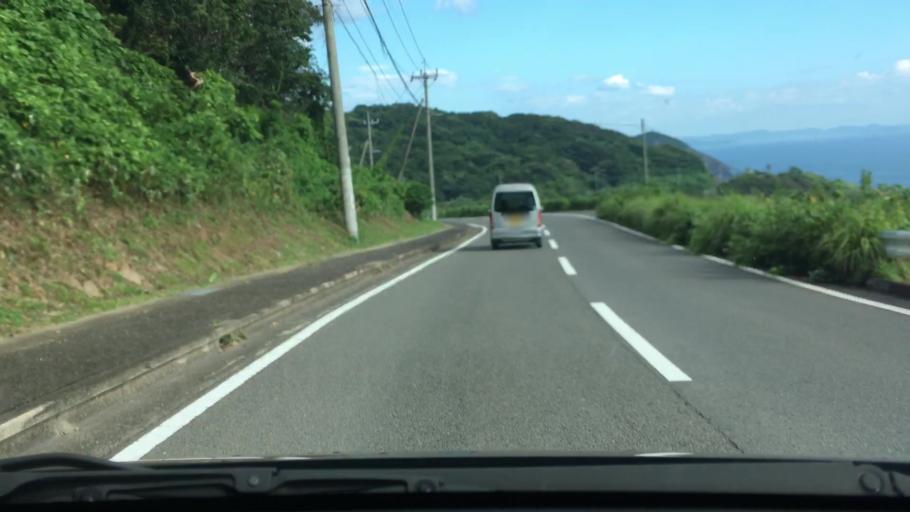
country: JP
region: Nagasaki
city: Togitsu
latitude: 32.8492
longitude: 129.6923
